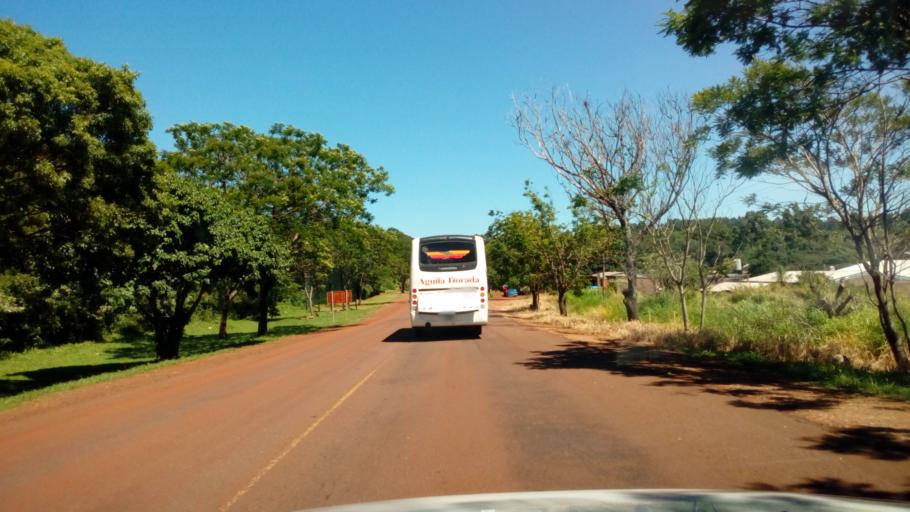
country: AR
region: Misiones
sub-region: Departamento de Leandro N. Alem
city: Leandro N. Alem
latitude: -27.6022
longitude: -55.3428
